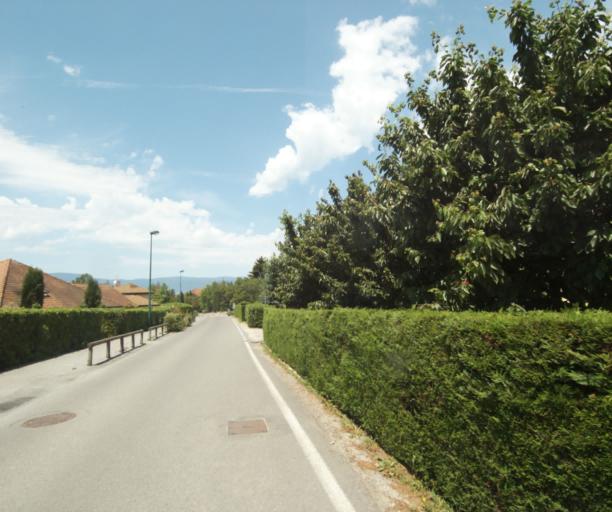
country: FR
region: Rhone-Alpes
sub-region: Departement de la Haute-Savoie
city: Messery
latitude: 46.3657
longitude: 6.3243
